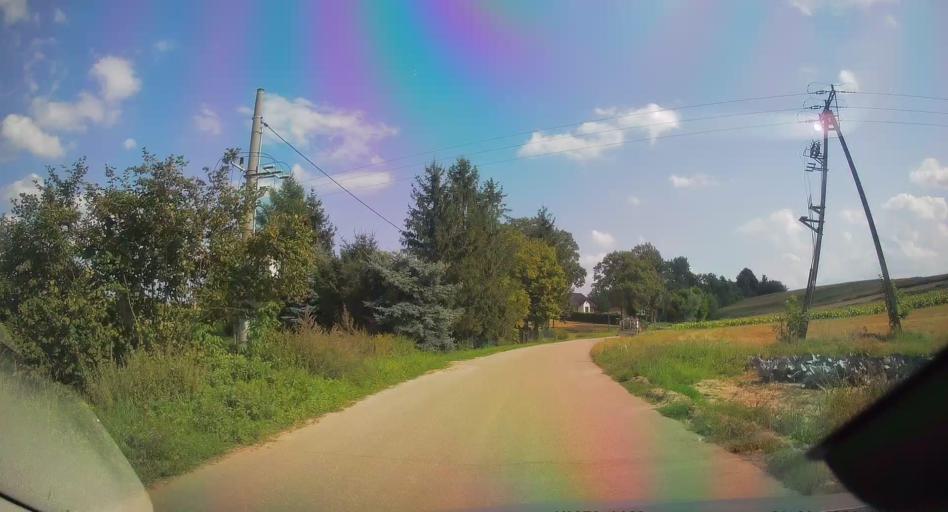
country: PL
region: Lesser Poland Voivodeship
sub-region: Powiat bochenski
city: Dziewin
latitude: 50.1571
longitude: 20.4605
